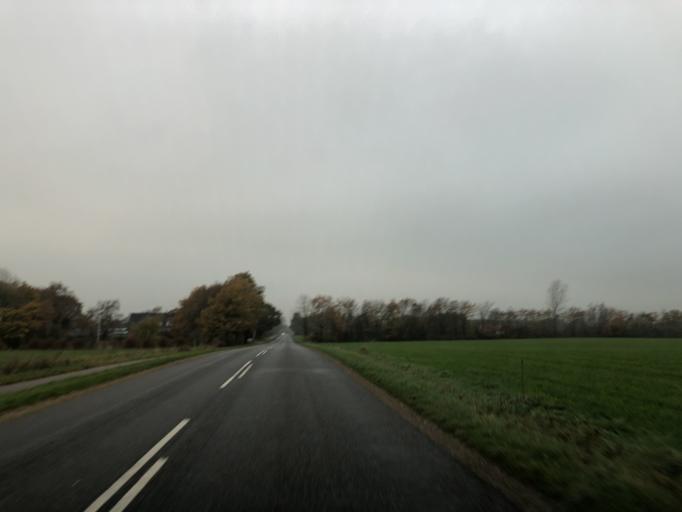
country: DK
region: Central Jutland
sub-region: Herning Kommune
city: Vildbjerg
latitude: 56.2106
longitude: 8.7539
